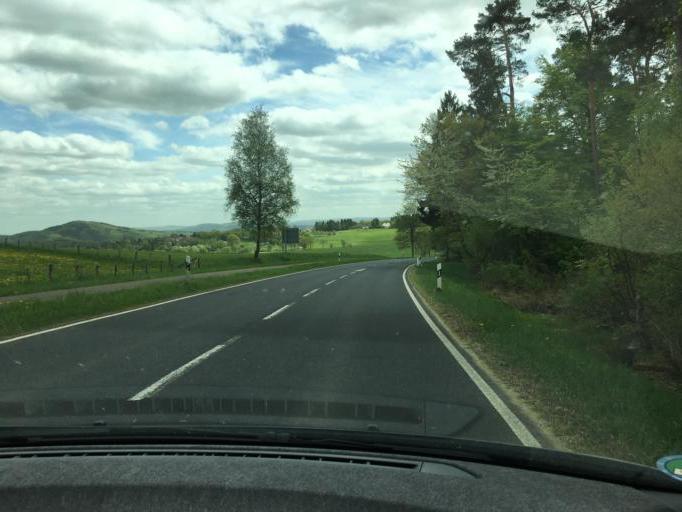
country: DE
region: Rheinland-Pfalz
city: Kirchsahr
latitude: 50.5297
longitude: 6.8497
